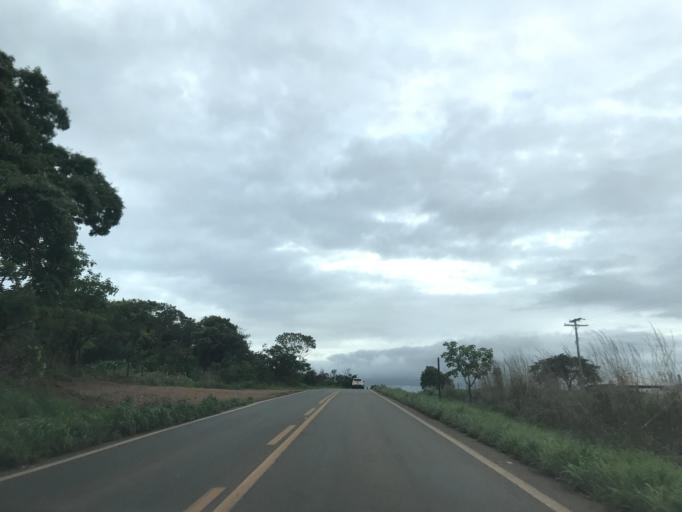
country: BR
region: Goias
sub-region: Luziania
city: Luziania
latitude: -16.2761
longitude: -47.9934
